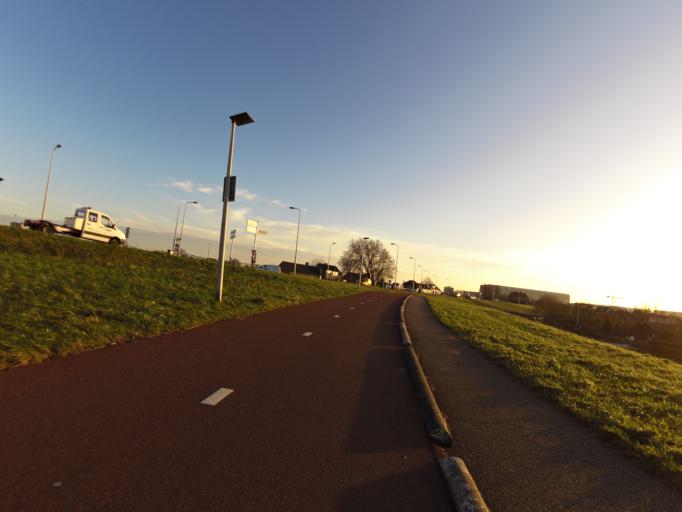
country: NL
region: South Holland
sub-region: Gemeente Capelle aan den IJssel
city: Capelle-West
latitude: 51.9170
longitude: 4.5764
